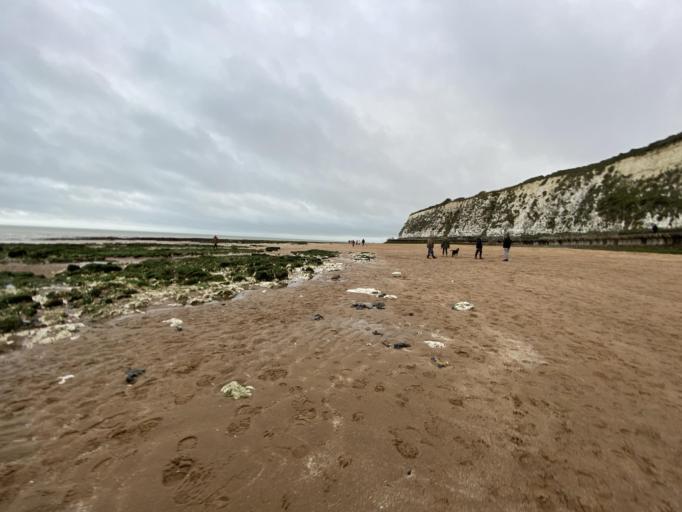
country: GB
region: England
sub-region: Kent
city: Broadstairs
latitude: 51.3525
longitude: 1.4429
